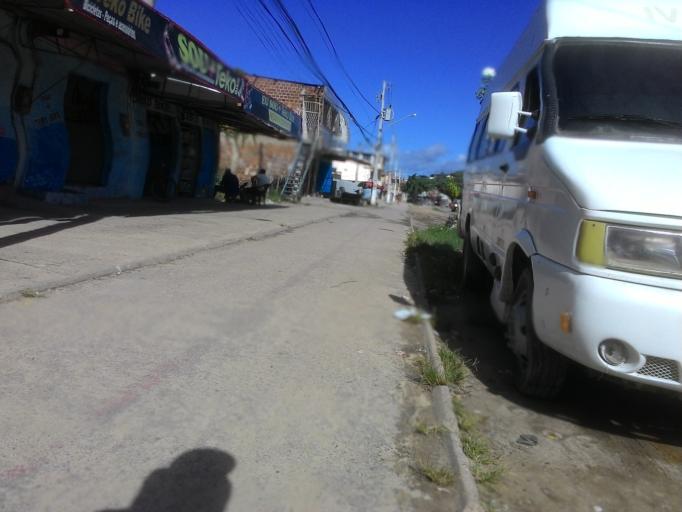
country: BR
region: Pernambuco
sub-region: Olinda
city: Olinda
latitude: -7.9803
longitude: -34.8580
